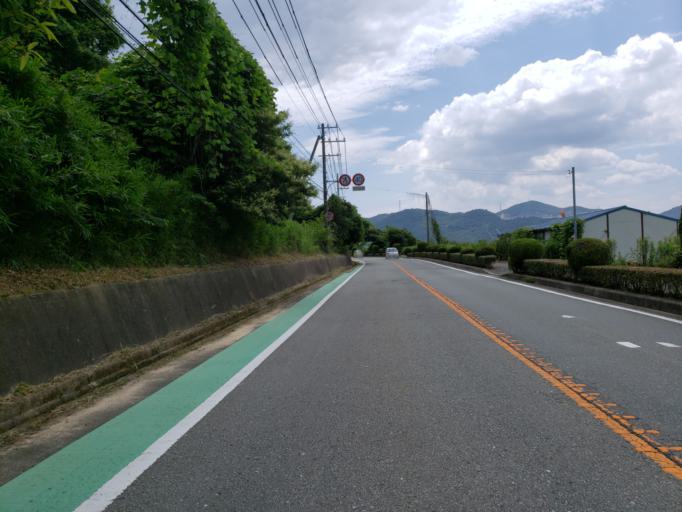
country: JP
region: Hyogo
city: Aioi
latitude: 34.7852
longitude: 134.4775
